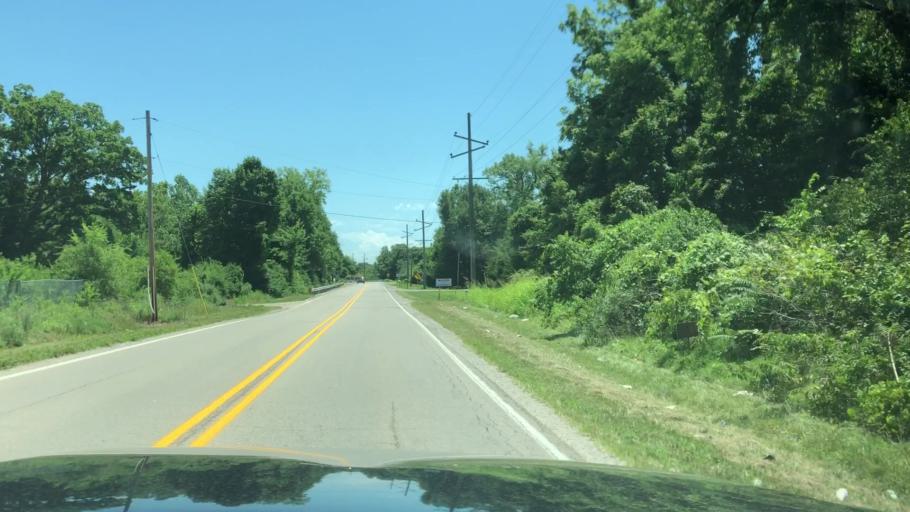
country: US
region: Illinois
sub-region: Saint Clair County
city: Alorton
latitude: 38.5514
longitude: -90.0748
